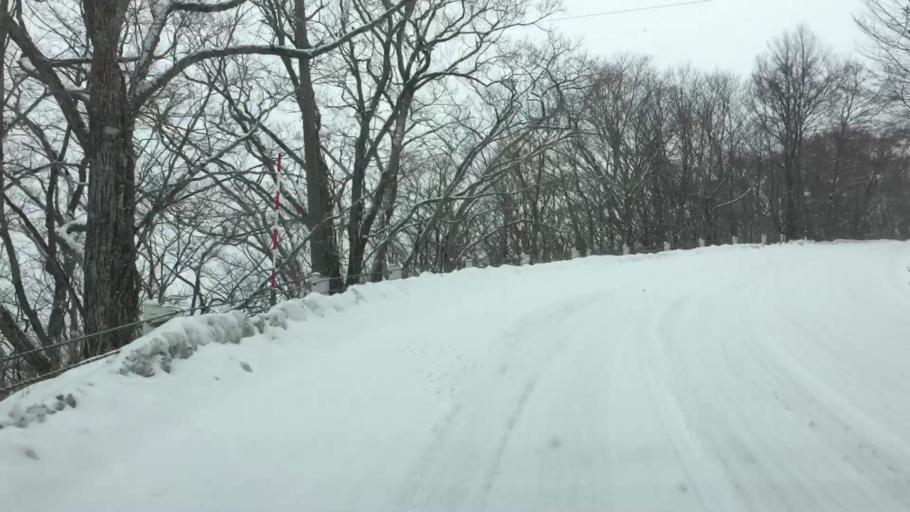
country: JP
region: Tochigi
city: Imaichi
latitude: 36.9082
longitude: 139.7377
